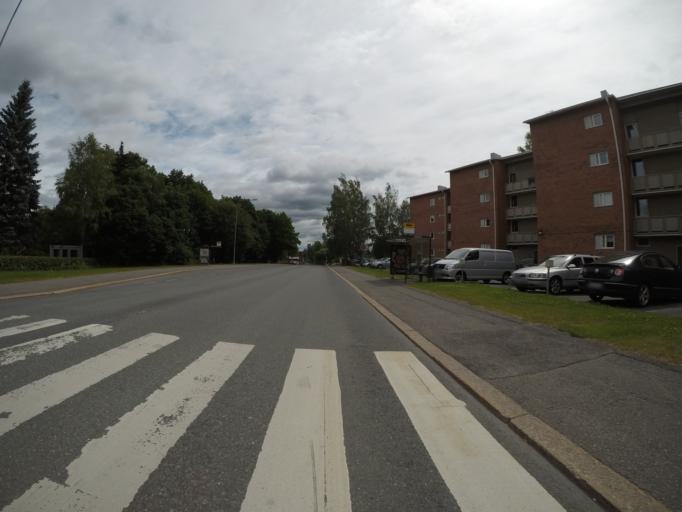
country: FI
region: Haeme
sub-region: Haemeenlinna
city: Haemeenlinna
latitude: 61.0039
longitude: 24.4864
